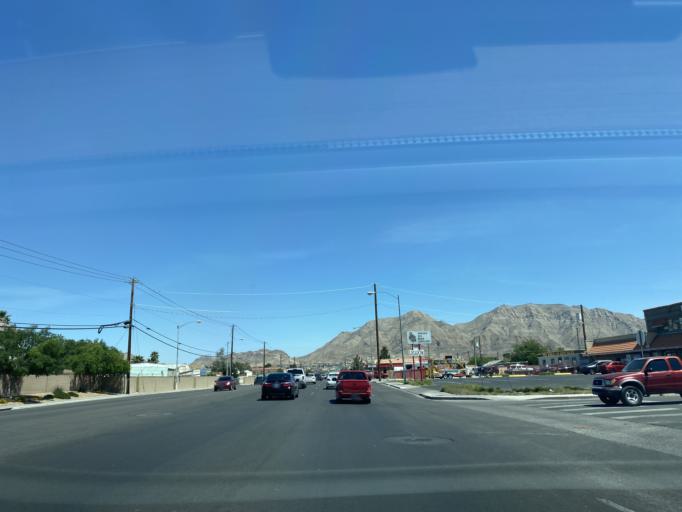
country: US
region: Nevada
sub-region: Clark County
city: Sunrise Manor
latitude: 36.1962
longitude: -115.0599
